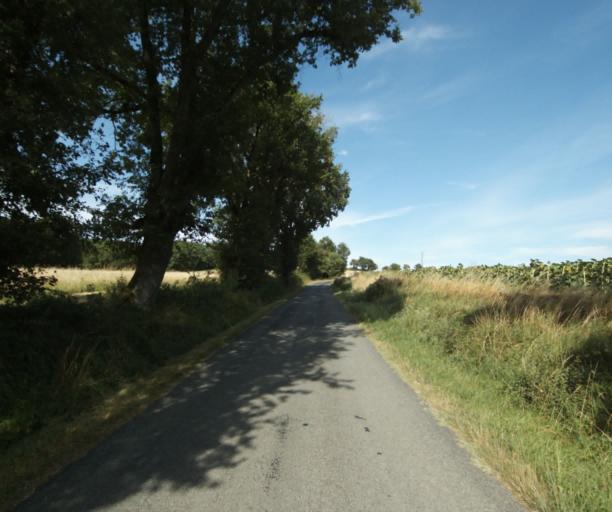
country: FR
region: Midi-Pyrenees
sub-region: Departement du Tarn
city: Puylaurens
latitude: 43.5259
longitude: 2.0480
